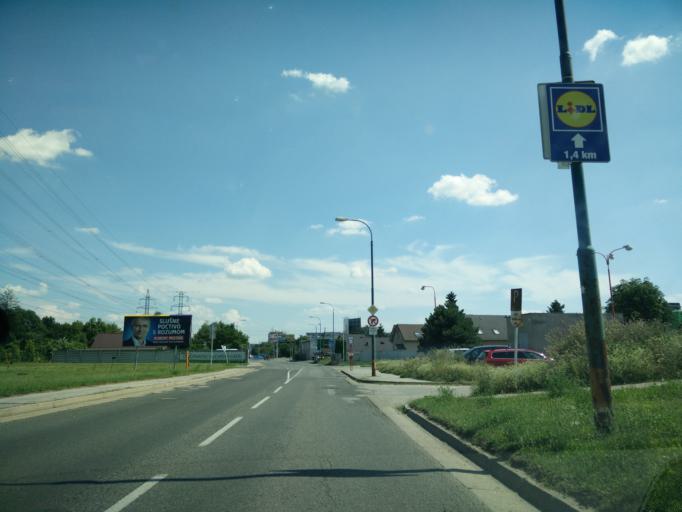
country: SK
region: Bratislavsky
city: Bratislava
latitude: 48.1793
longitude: 17.1654
